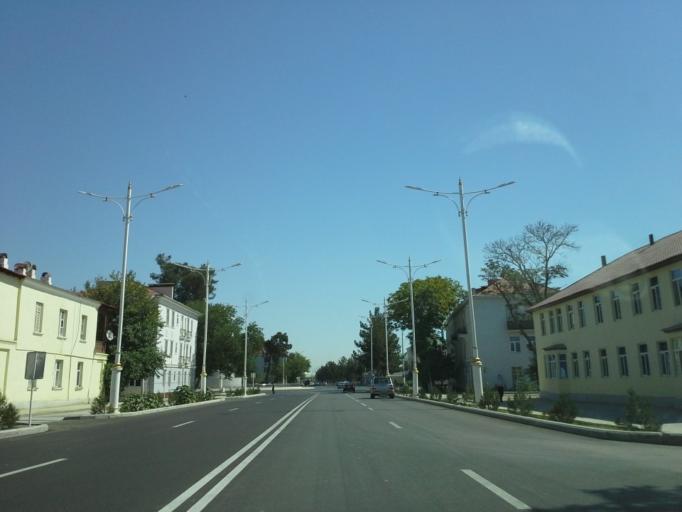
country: TM
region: Ahal
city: Ashgabat
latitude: 37.9564
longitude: 58.3579
